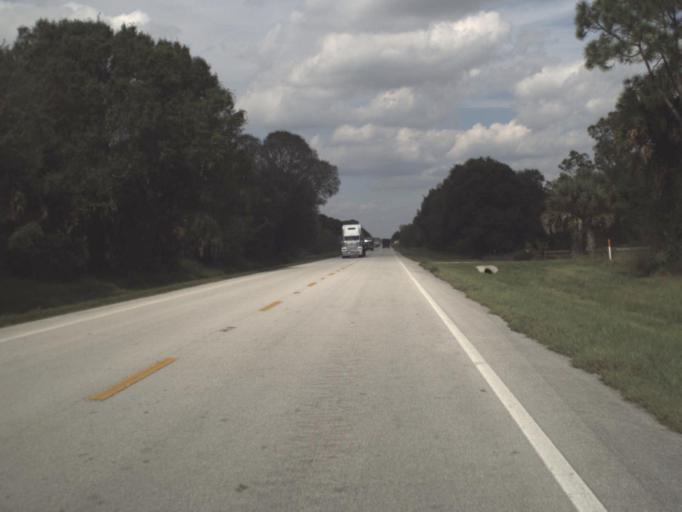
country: US
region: Florida
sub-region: Okeechobee County
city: Cypress Quarters
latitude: 27.3251
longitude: -80.8243
